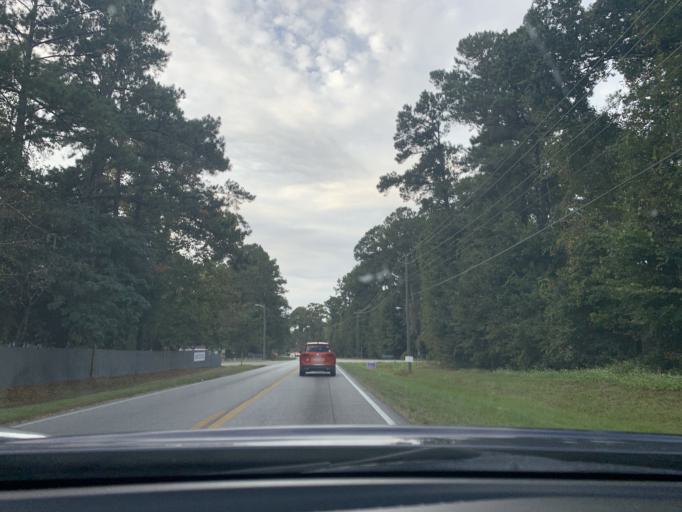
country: US
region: Georgia
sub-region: Chatham County
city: Georgetown
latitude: 32.0332
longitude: -81.2528
